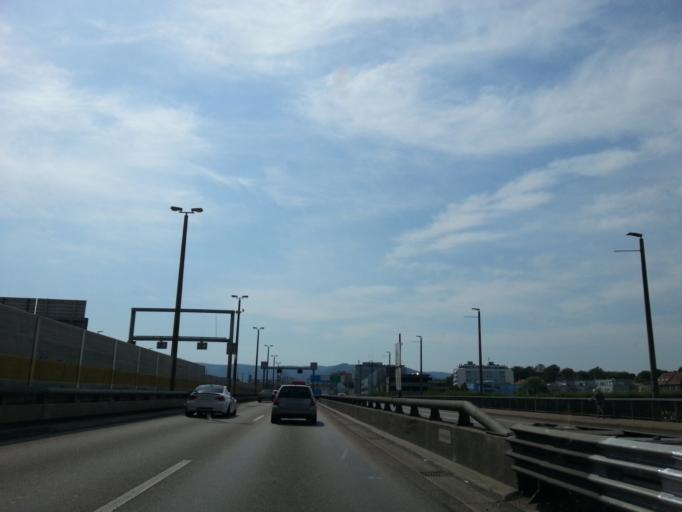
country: CH
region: Basel-Landschaft
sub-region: Bezirk Arlesheim
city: Birsfelden
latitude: 47.5588
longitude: 7.6133
